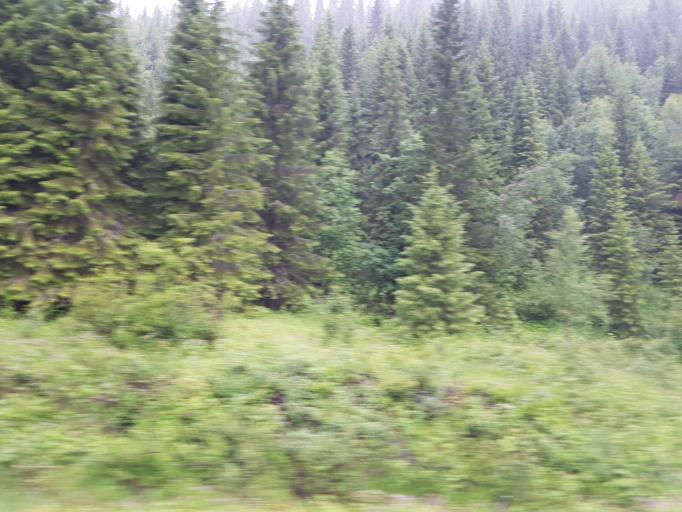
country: NO
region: Sor-Trondelag
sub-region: Selbu
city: Mebonden
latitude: 63.3283
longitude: 11.0874
